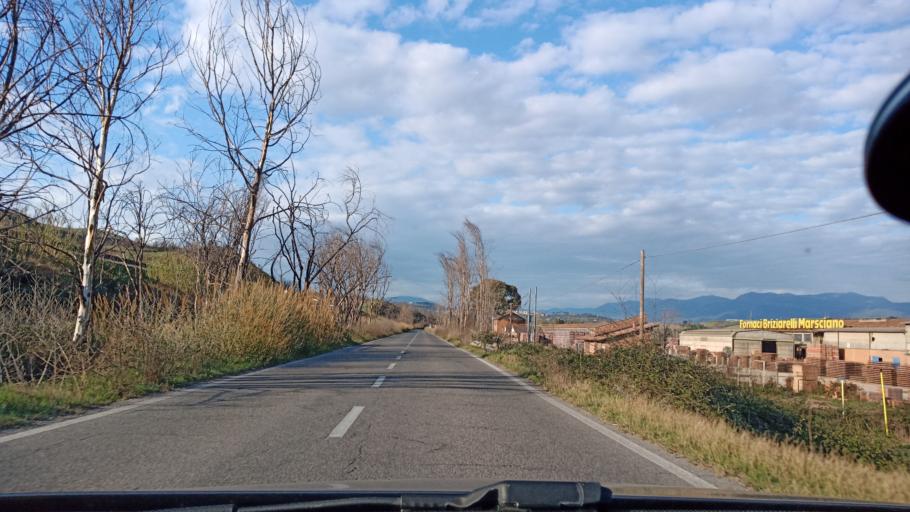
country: IT
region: Latium
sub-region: Citta metropolitana di Roma Capitale
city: Civitella San Paolo
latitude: 42.1911
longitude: 12.6041
